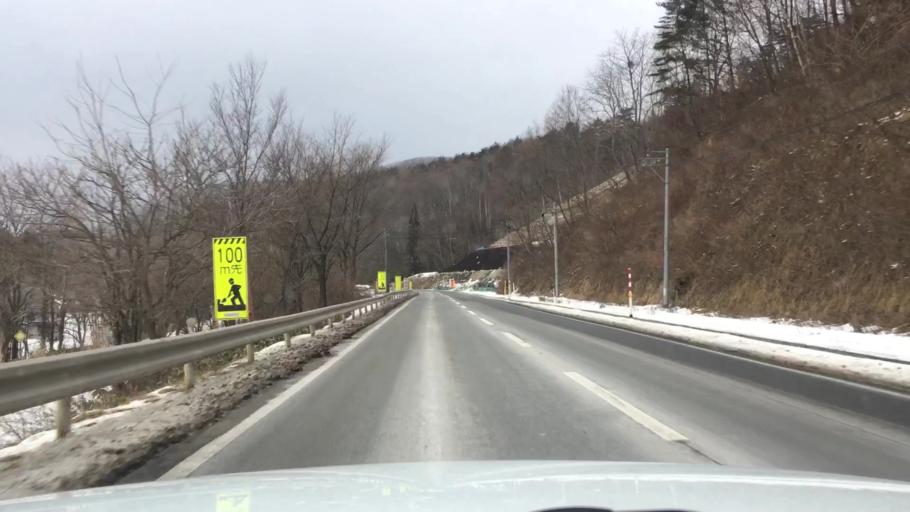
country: JP
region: Iwate
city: Morioka-shi
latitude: 39.6347
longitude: 141.4394
